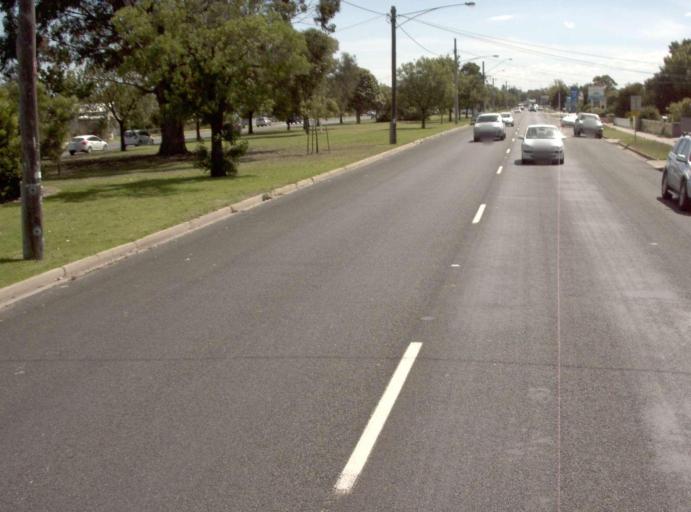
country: AU
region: Victoria
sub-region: East Gippsland
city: Bairnsdale
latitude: -37.8279
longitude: 147.6214
